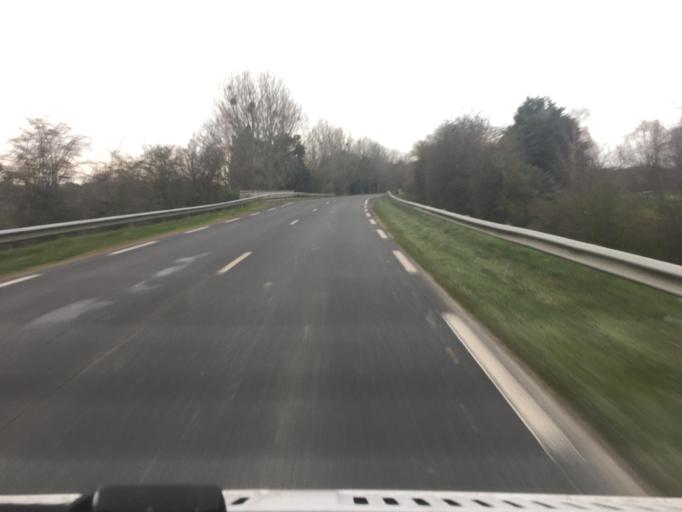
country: FR
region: Lower Normandy
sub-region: Departement du Calvados
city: Cabourg
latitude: 49.2753
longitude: -0.1286
